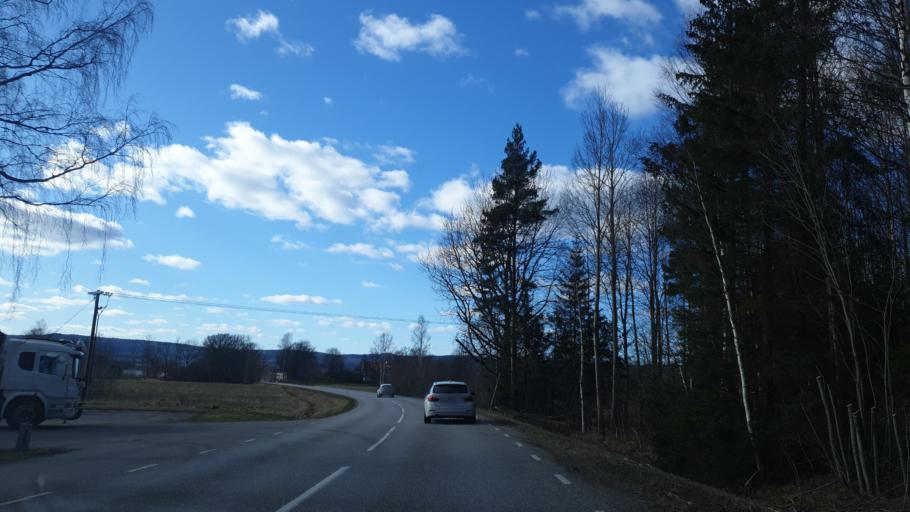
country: SE
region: OErebro
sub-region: Orebro Kommun
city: Garphyttan
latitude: 59.3376
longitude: 15.0691
